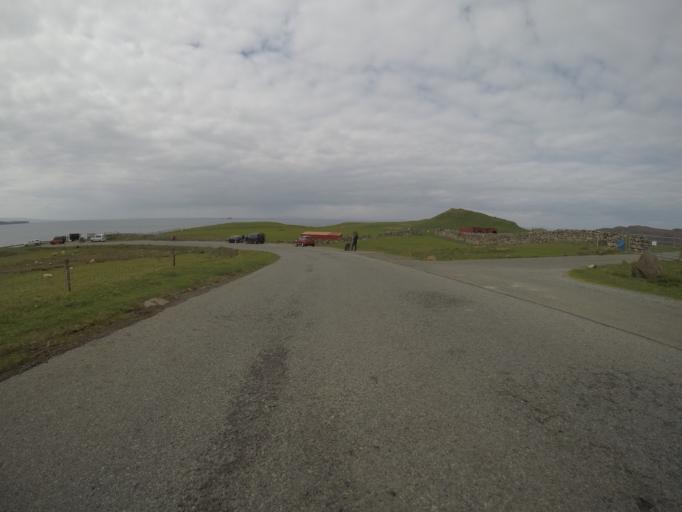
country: GB
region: Scotland
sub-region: Highland
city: Portree
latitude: 57.6820
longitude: -6.3438
